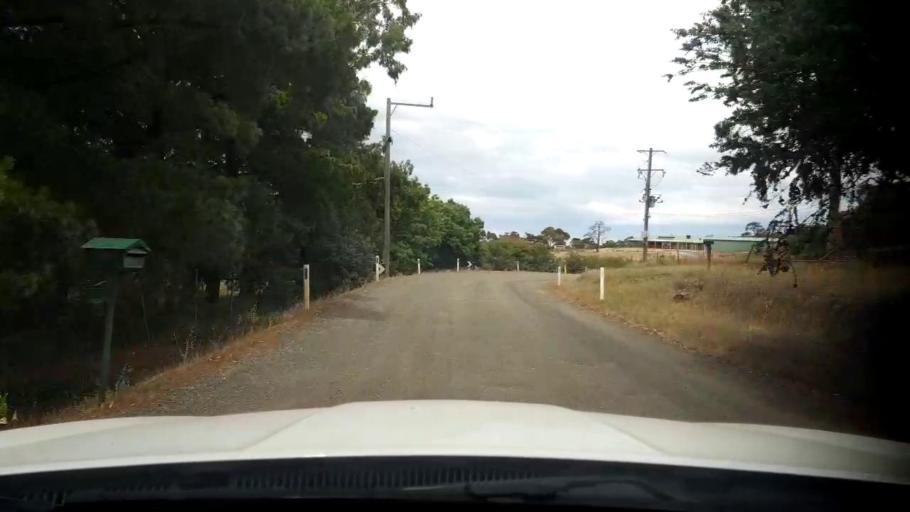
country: AU
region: Victoria
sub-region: Whittlesea
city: Whittlesea
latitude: -37.4897
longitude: 145.0639
